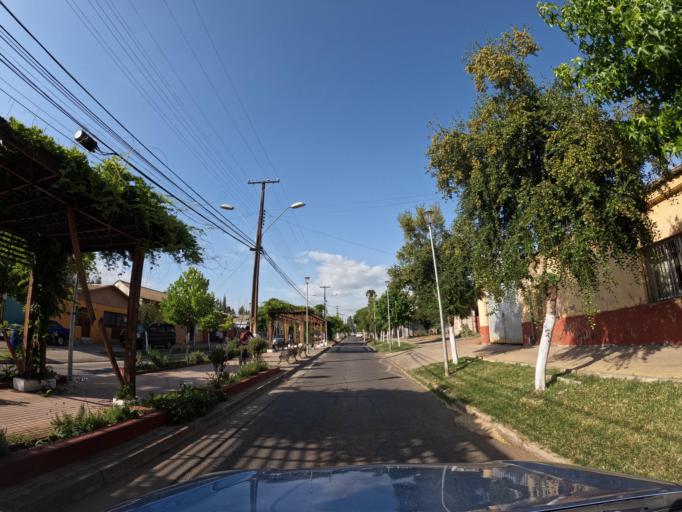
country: CL
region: Maule
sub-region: Provincia de Curico
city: Molina
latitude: -35.2846
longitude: -71.2609
